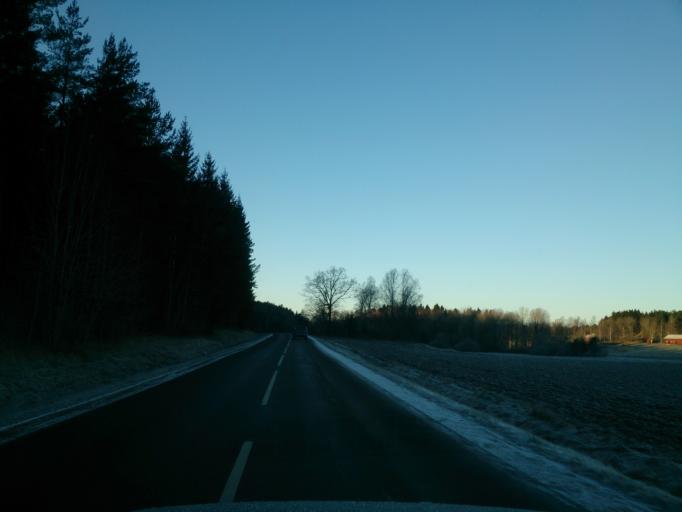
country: SE
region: OEstergoetland
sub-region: Norrkopings Kommun
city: Kimstad
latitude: 58.3840
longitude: 16.0154
